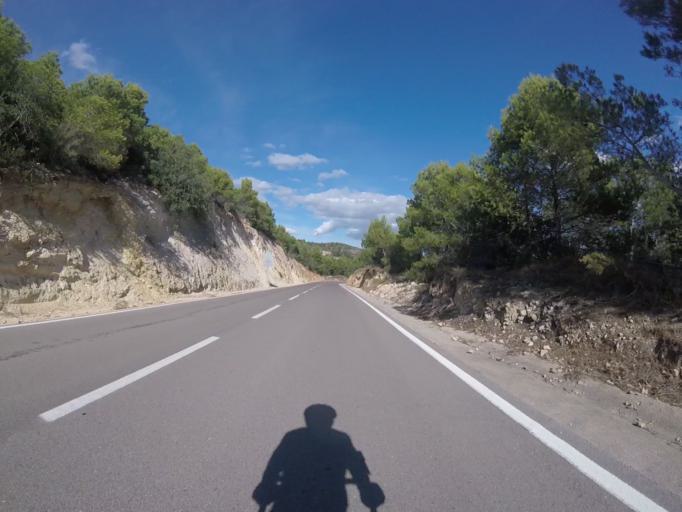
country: ES
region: Valencia
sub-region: Provincia de Castello
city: Alcala de Xivert
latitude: 40.3012
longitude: 0.1892
